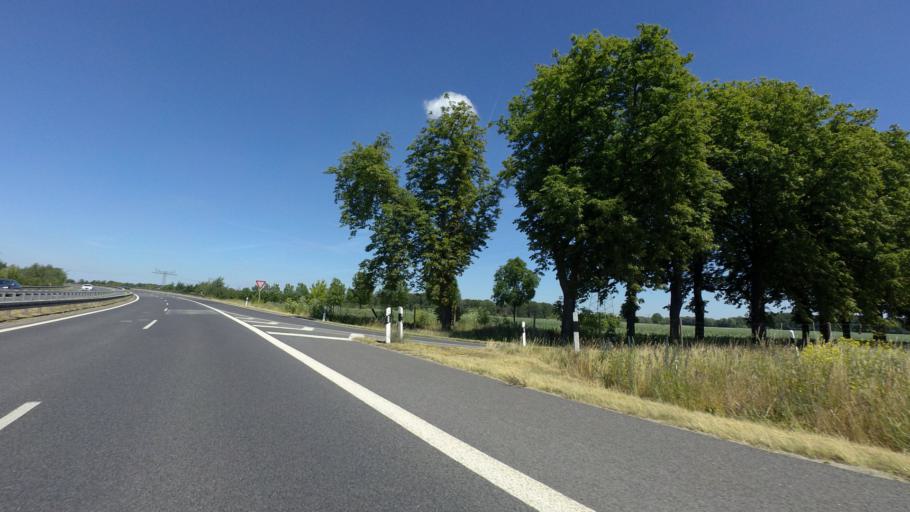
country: DE
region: Brandenburg
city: Rangsdorf
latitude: 52.3182
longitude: 13.4500
